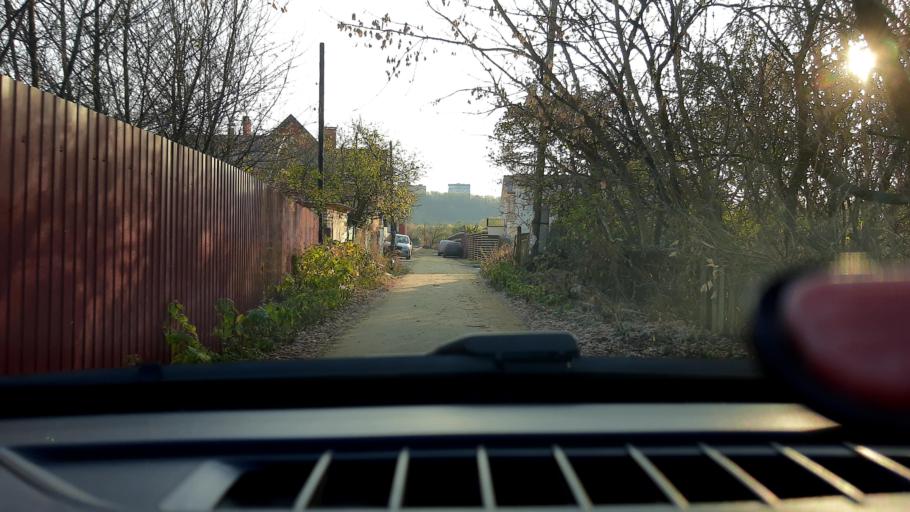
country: RU
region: Nizjnij Novgorod
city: Nizhniy Novgorod
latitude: 56.2711
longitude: 43.9529
